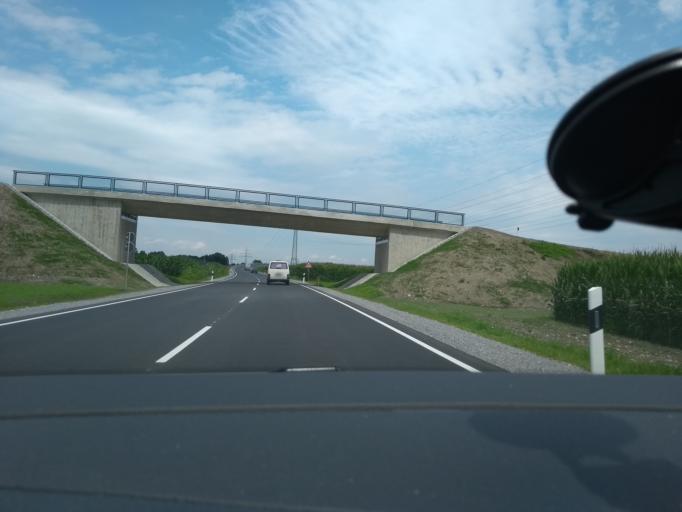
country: DE
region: Bavaria
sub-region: Upper Bavaria
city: Grosskarolinenfeld
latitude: 47.8923
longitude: 12.1120
